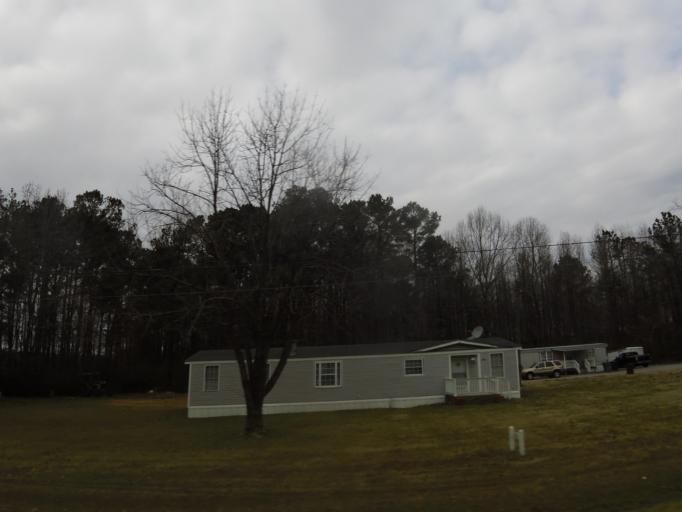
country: US
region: North Carolina
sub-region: Hertford County
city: Murfreesboro
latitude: 36.3185
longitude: -77.2413
